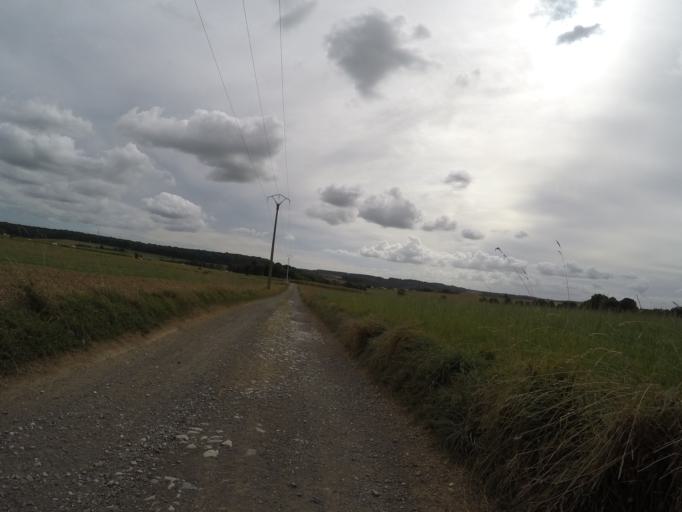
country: BE
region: Wallonia
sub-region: Province de Namur
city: Dinant
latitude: 50.2917
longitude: 4.9856
